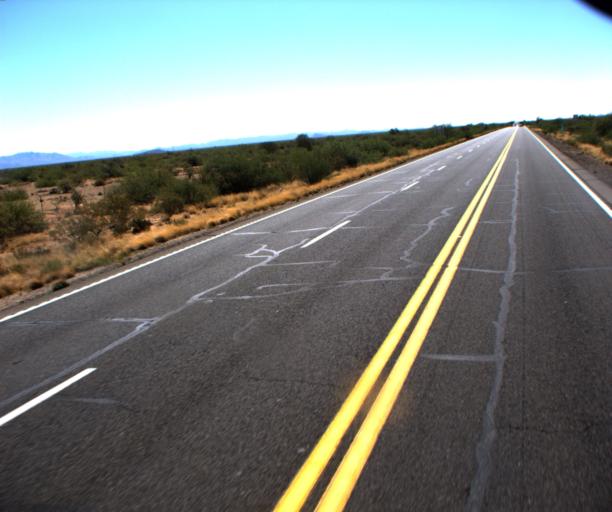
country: US
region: Arizona
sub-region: Yavapai County
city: Congress
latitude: 34.1325
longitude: -112.9637
